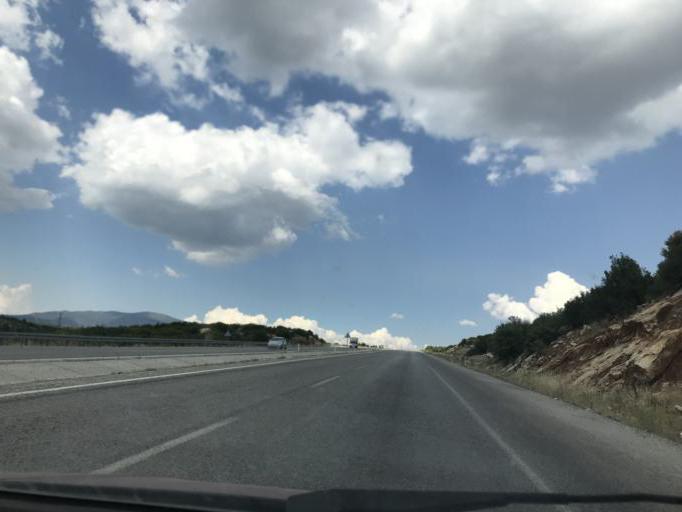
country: TR
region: Denizli
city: Tavas
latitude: 37.5858
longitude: 29.1031
